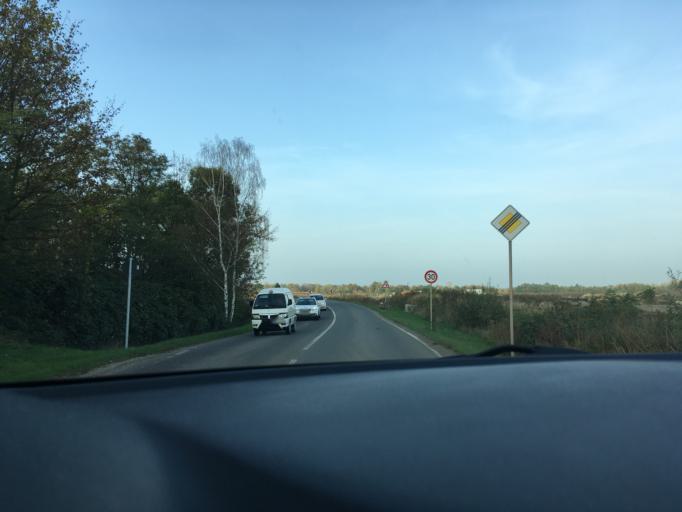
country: DE
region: Saxony
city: Rotha
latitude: 51.2038
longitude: 12.4165
